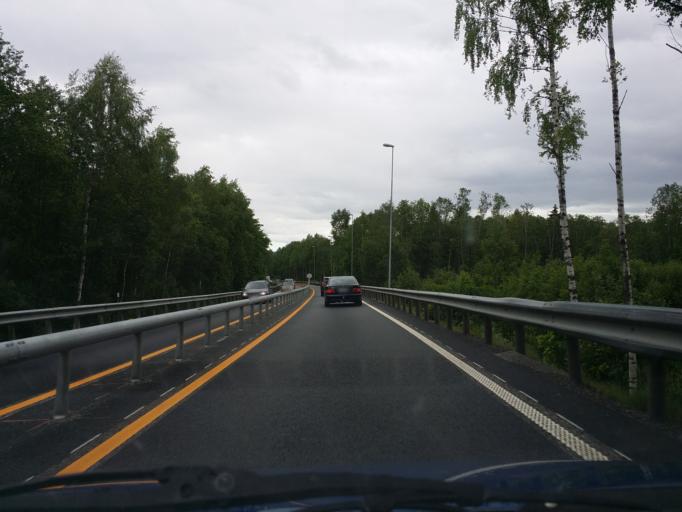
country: NO
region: Hedmark
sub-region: Ringsaker
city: Moelv
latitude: 60.9675
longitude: 10.6030
